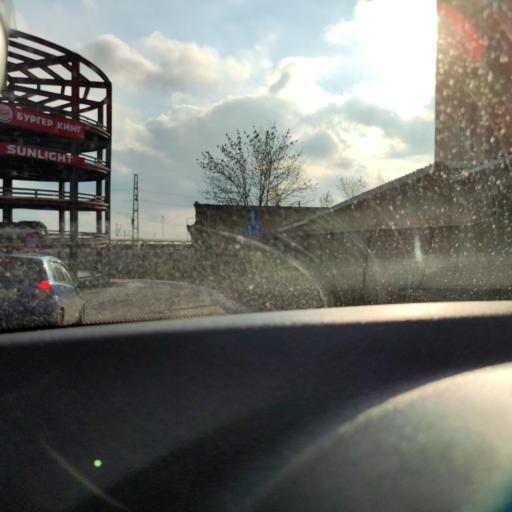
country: RU
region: Samara
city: Samara
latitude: 53.1865
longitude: 50.1247
